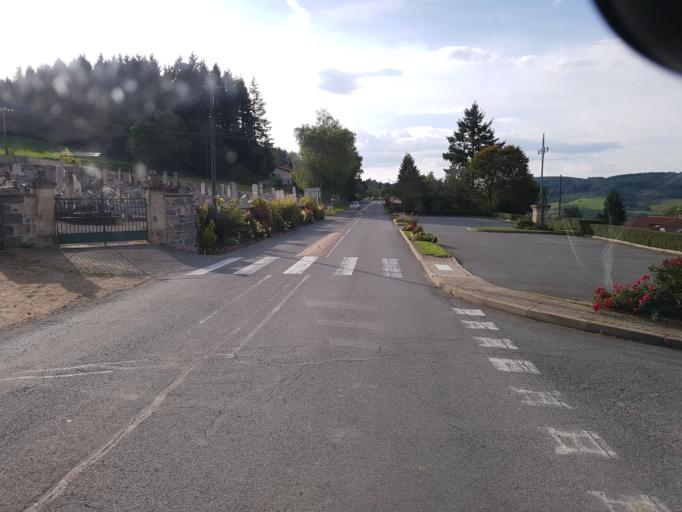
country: FR
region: Rhone-Alpes
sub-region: Departement de la Loire
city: Belmont-de-la-Loire
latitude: 46.1900
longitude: 4.4378
